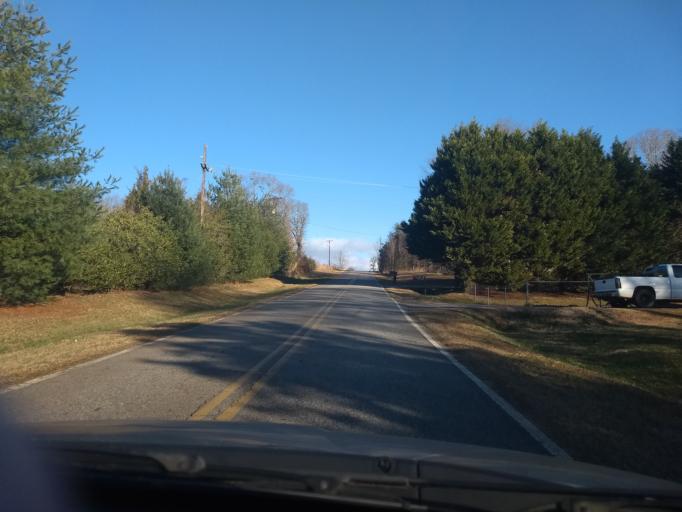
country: US
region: South Carolina
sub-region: Greenville County
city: Greer
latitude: 35.0269
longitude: -82.2017
